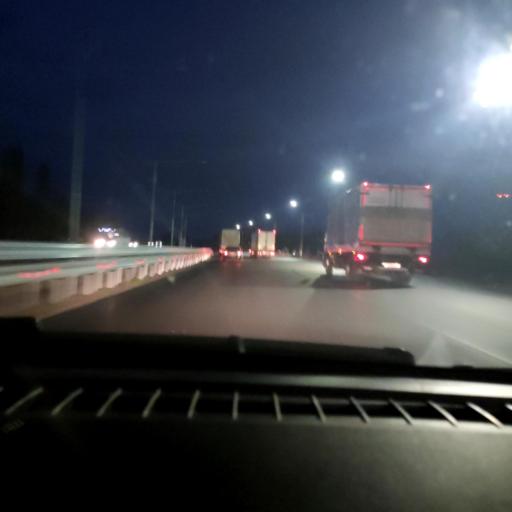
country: RU
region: Voronezj
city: Ramon'
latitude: 51.9921
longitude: 39.2190
